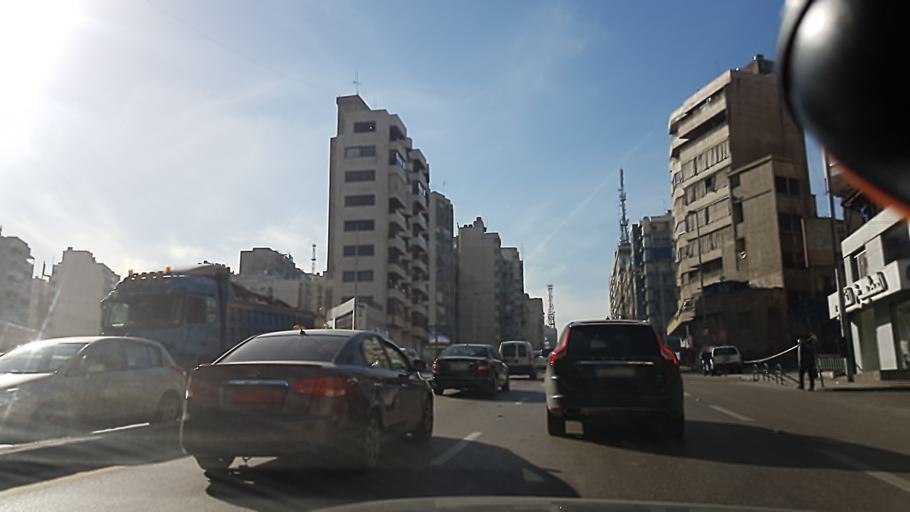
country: LB
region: Beyrouth
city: Beirut
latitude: 33.8892
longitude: 35.4998
